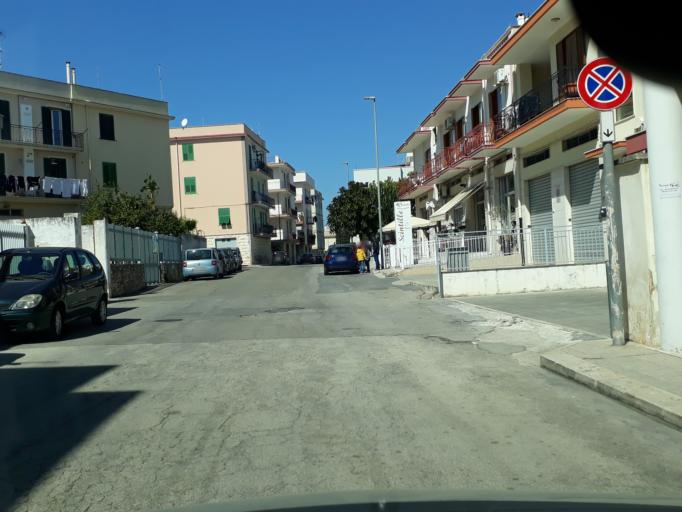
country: IT
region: Apulia
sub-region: Provincia di Brindisi
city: Fasano
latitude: 40.8369
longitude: 17.3643
